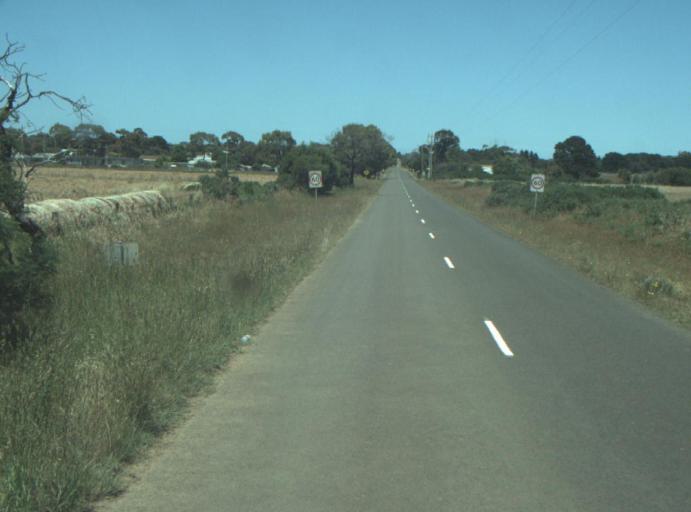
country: AU
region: Victoria
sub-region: Queenscliffe
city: Queenscliff
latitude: -38.1717
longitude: 144.7017
